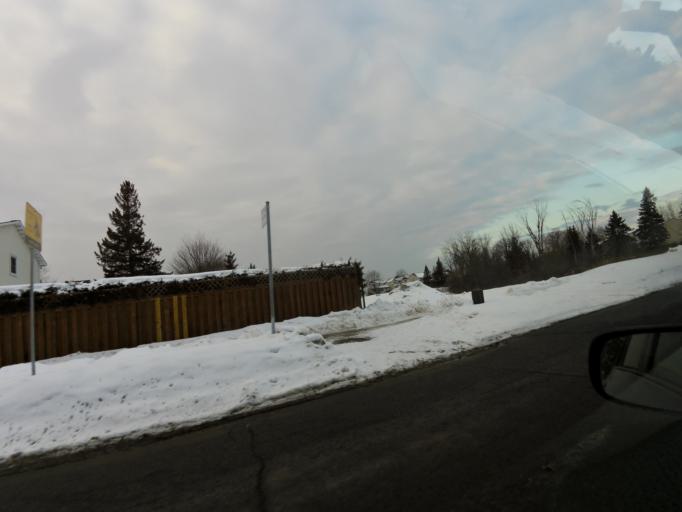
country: CA
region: Quebec
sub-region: Outaouais
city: Gatineau
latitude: 45.4738
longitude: -75.5387
